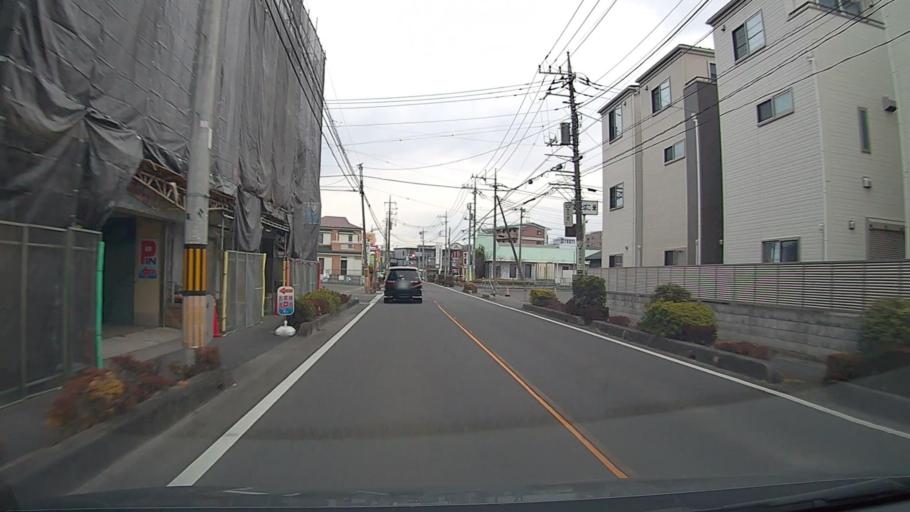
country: JP
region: Saitama
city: Wako
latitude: 35.8308
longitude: 139.6410
